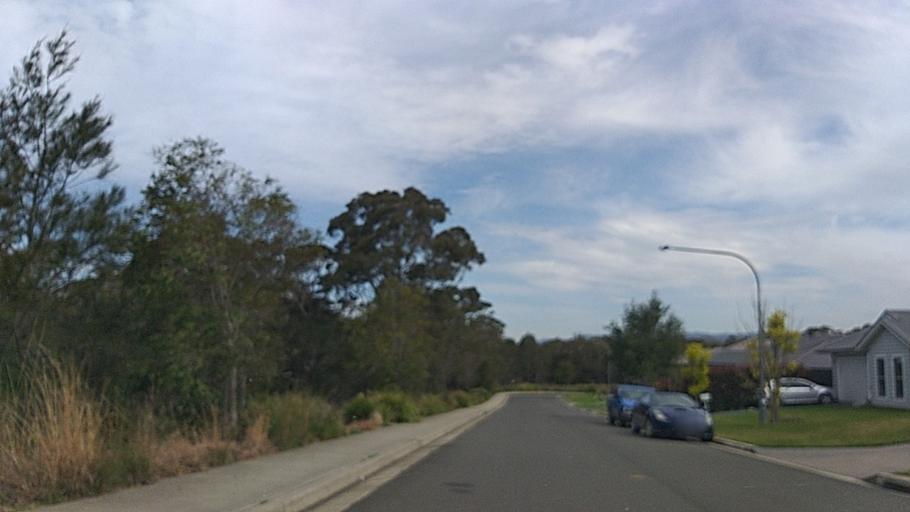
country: AU
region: New South Wales
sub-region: Wollongong
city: Dapto
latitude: -34.4951
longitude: 150.7631
